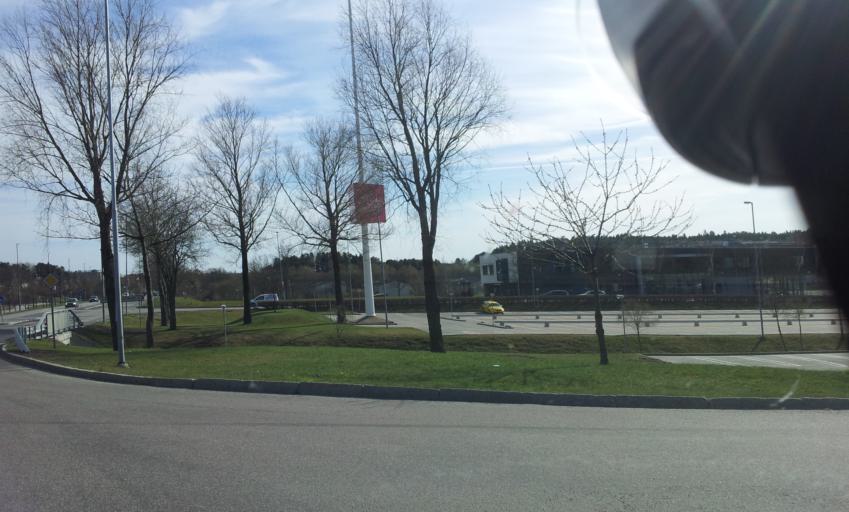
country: SE
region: Stockholm
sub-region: Upplands Vasby Kommun
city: Upplands Vaesby
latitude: 59.5189
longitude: 17.9179
